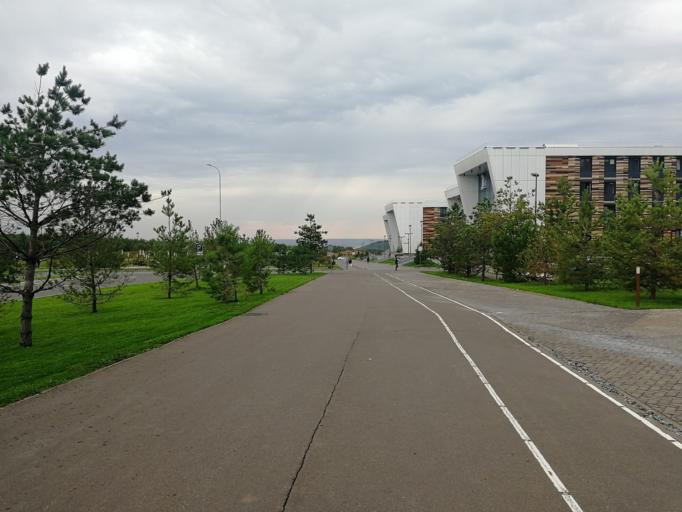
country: RU
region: Tatarstan
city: Sviyazhsk
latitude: 55.7531
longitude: 48.7422
